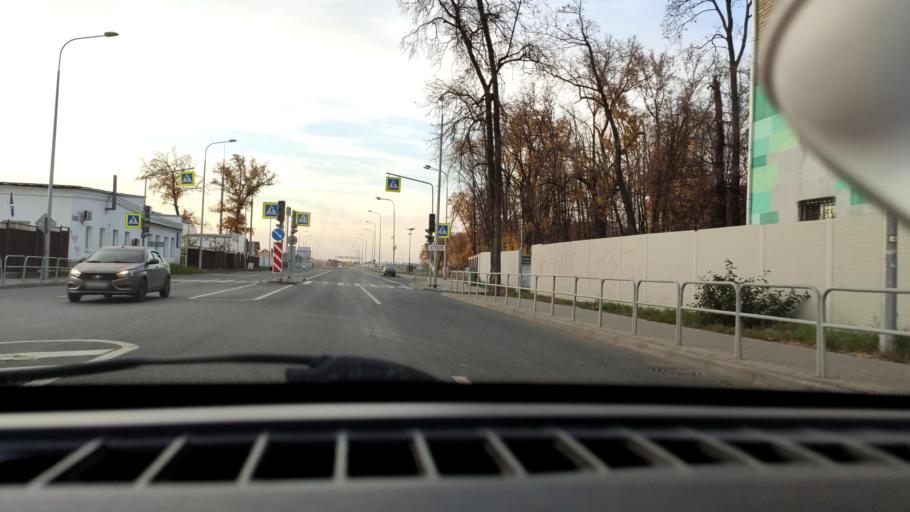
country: RU
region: Samara
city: Samara
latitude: 53.2673
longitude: 50.2397
